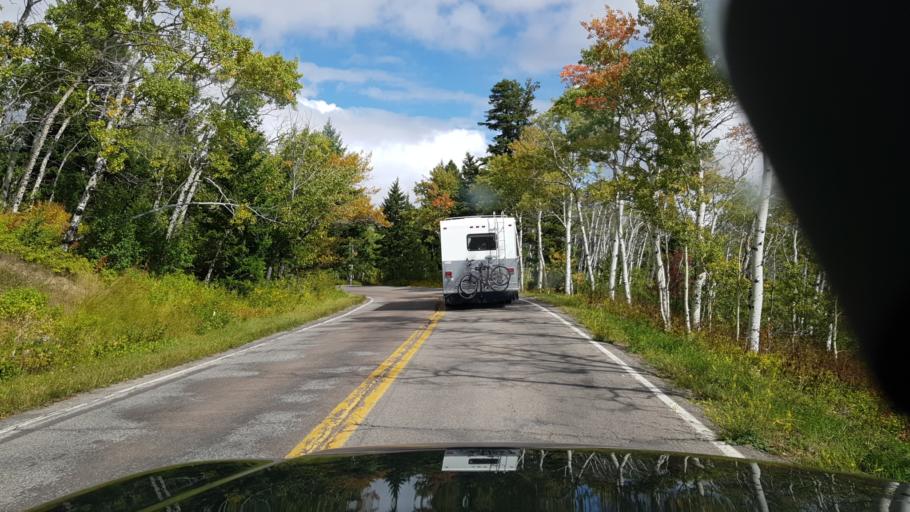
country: US
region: Montana
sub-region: Glacier County
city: South Browning
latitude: 48.4604
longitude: -113.2253
